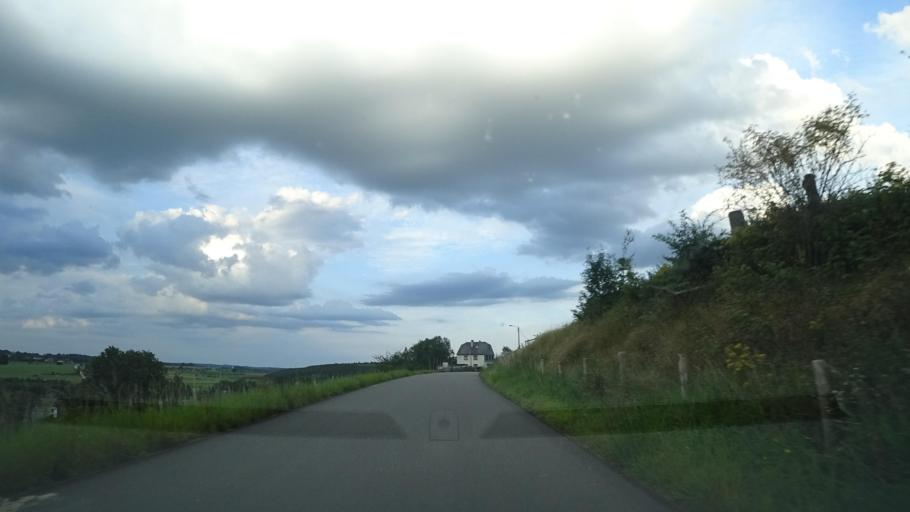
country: BE
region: Wallonia
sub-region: Province du Luxembourg
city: Bertrix
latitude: 49.8169
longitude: 5.3232
